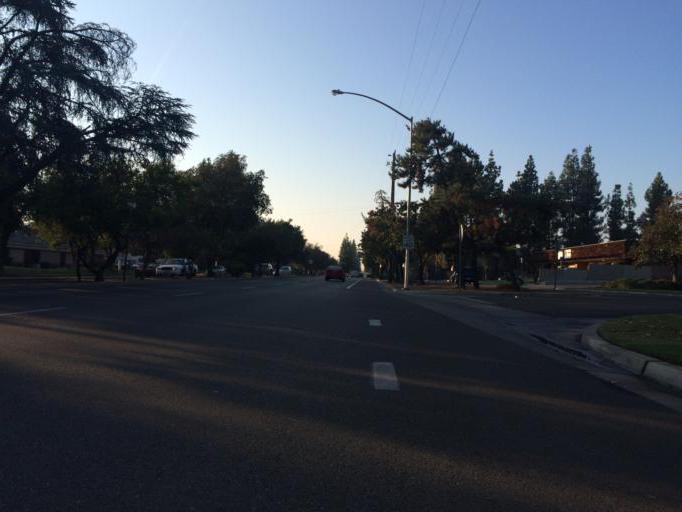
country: US
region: California
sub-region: Fresno County
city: Fresno
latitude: 36.7860
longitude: -119.7726
